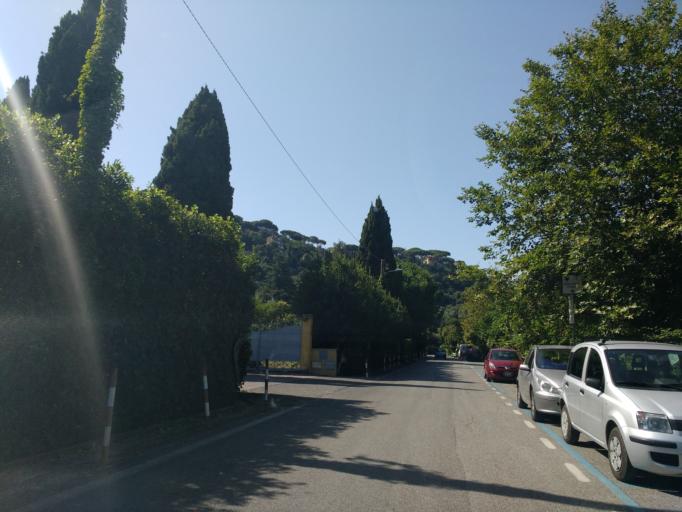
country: IT
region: Latium
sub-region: Citta metropolitana di Roma Capitale
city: Castel Gandolfo
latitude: 41.7499
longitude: 12.6531
